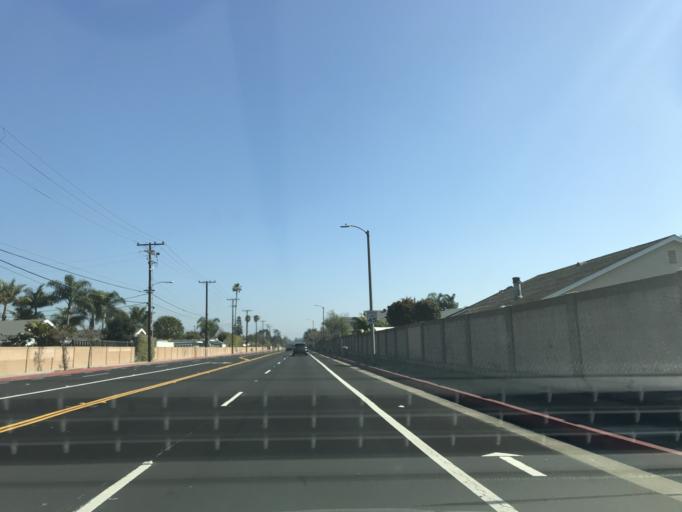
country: US
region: California
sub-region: Orange County
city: Fountain Valley
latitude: 33.6795
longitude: -117.9625
